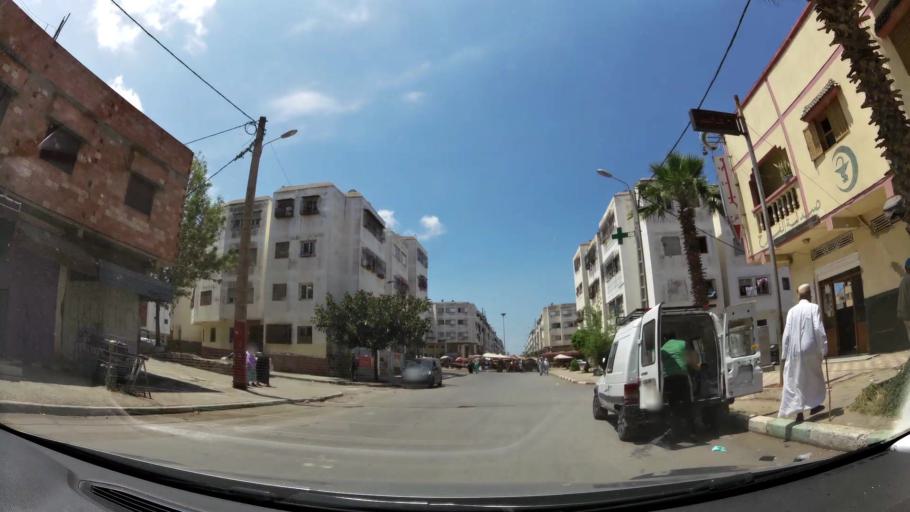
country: MA
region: Rabat-Sale-Zemmour-Zaer
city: Sale
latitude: 34.0694
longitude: -6.7855
